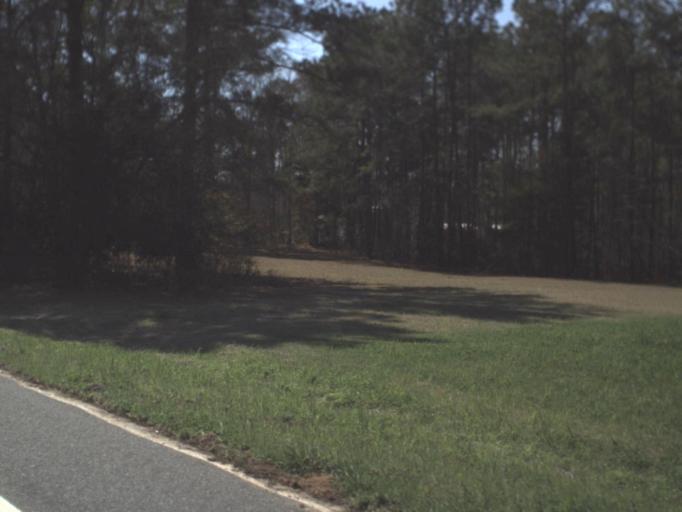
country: US
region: Florida
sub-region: Jackson County
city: Sneads
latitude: 30.6218
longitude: -85.0296
